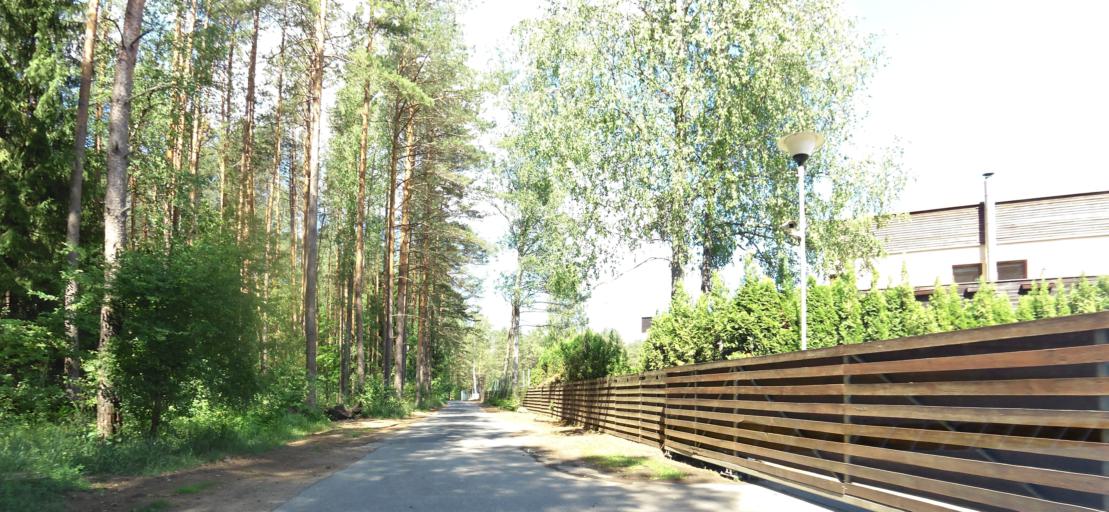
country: LT
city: Nemencine
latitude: 54.8132
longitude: 25.3902
